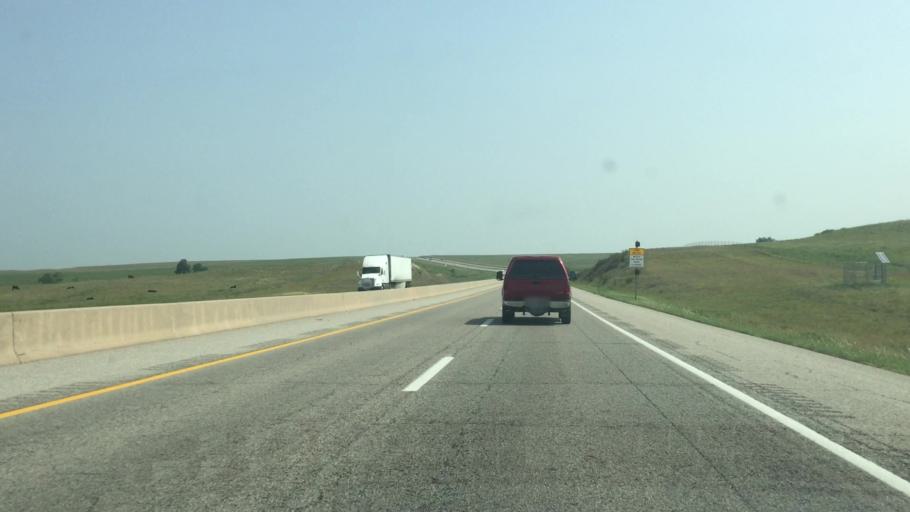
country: US
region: Kansas
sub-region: Chase County
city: Cottonwood Falls
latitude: 38.2884
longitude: -96.3597
